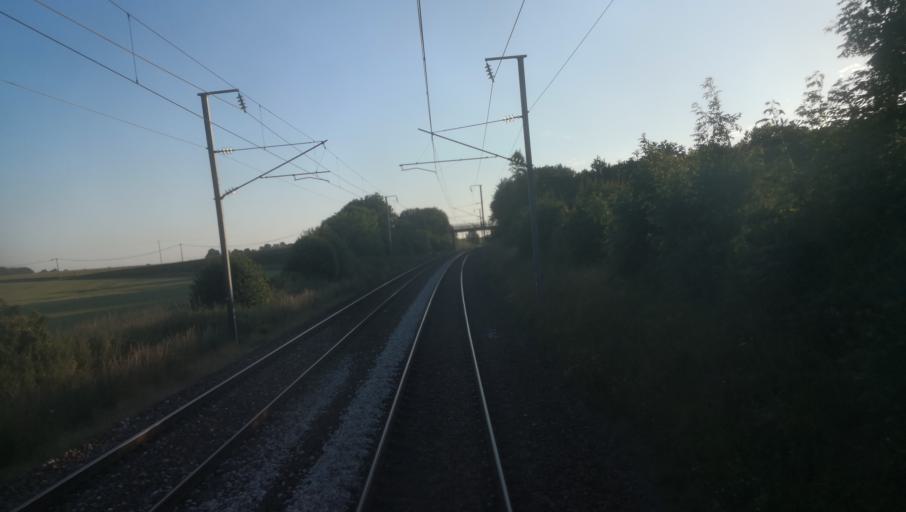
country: FR
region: Haute-Normandie
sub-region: Departement de l'Eure
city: Thiberville
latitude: 49.0815
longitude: 0.5056
